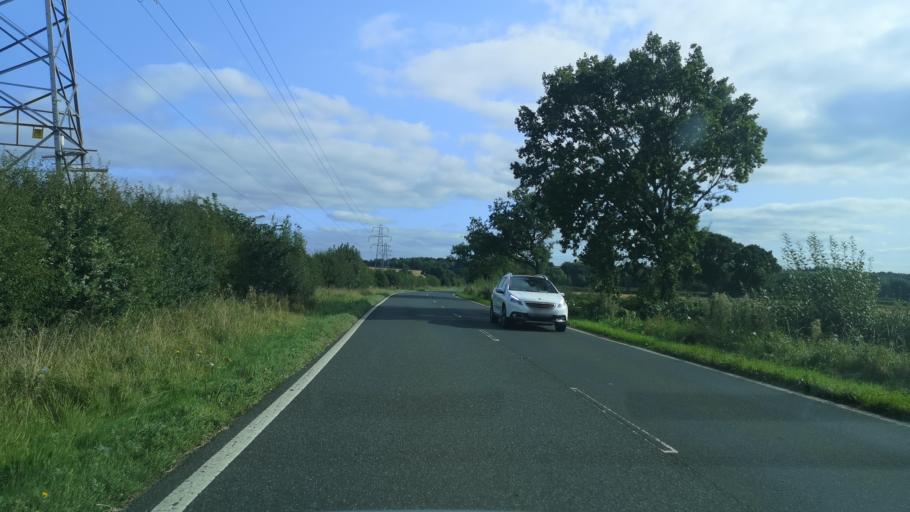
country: GB
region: England
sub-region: Barnsley
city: Royston
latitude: 53.6196
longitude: -1.4438
